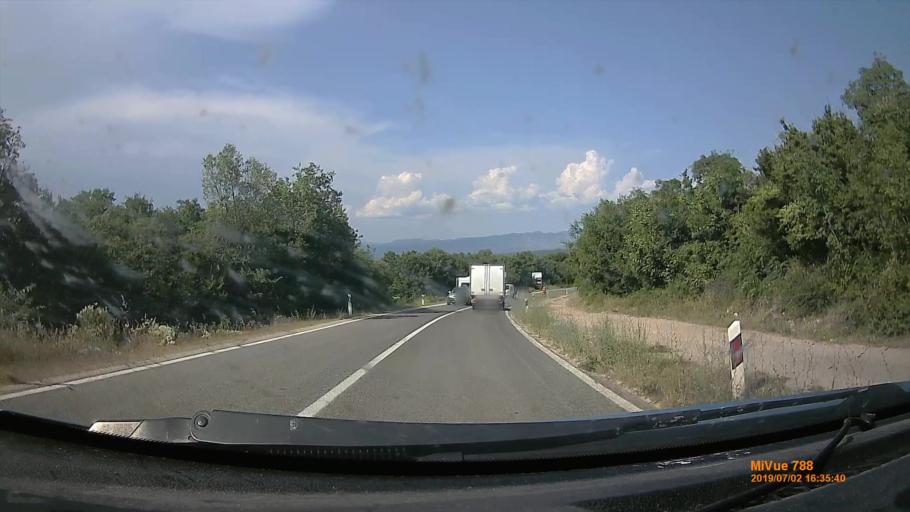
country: HR
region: Primorsko-Goranska
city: Njivice
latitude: 45.0898
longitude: 14.5153
